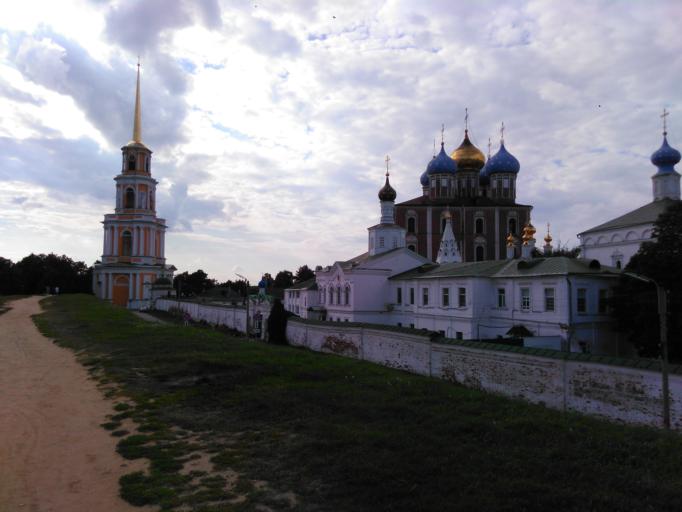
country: RU
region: Rjazan
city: Ryazan'
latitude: 54.6348
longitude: 39.7506
